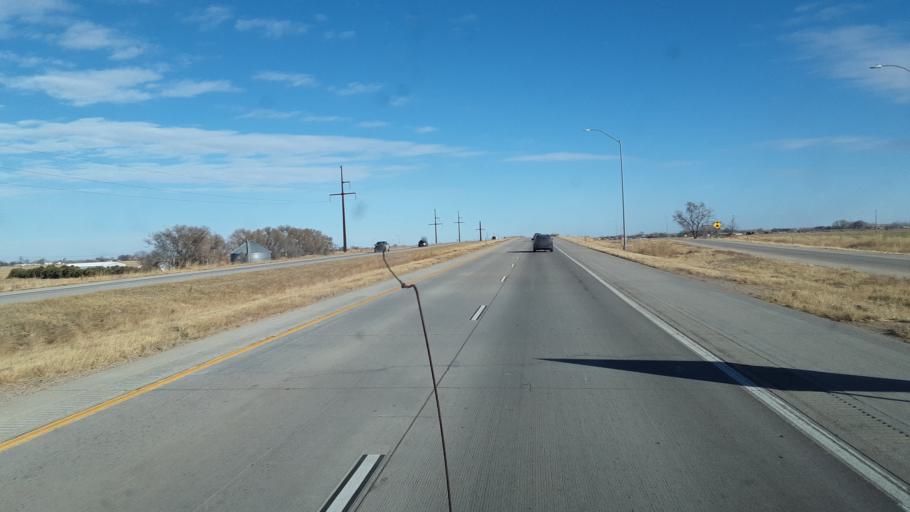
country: US
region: Colorado
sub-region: Morgan County
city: Brush
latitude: 40.2679
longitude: -103.7018
